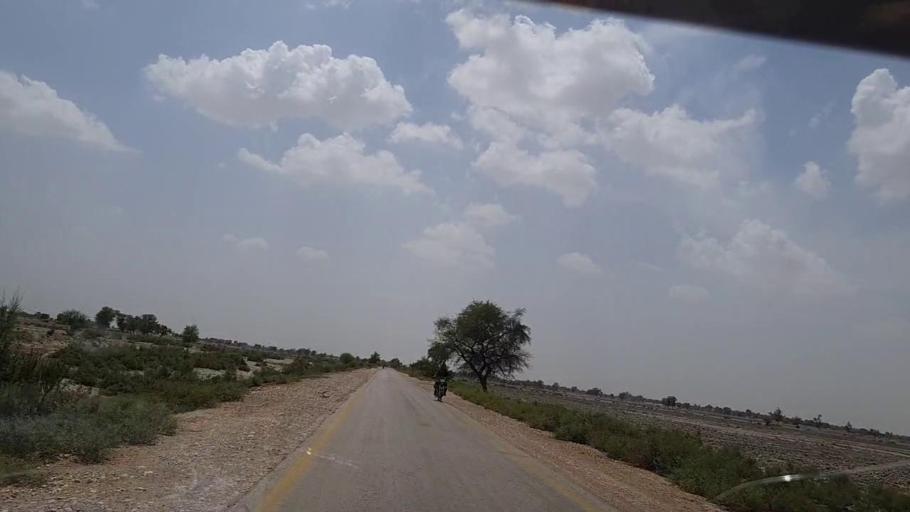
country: PK
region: Sindh
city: Bhan
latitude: 26.5414
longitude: 67.6513
